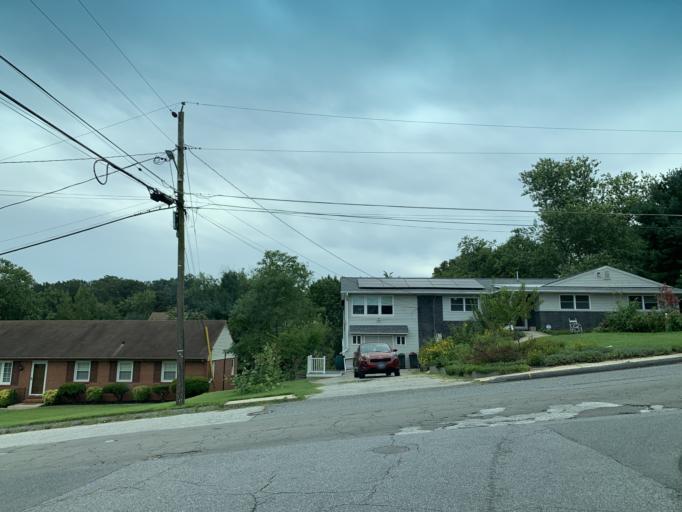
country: US
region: Maryland
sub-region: Baltimore County
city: Carney
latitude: 39.4095
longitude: -76.5231
